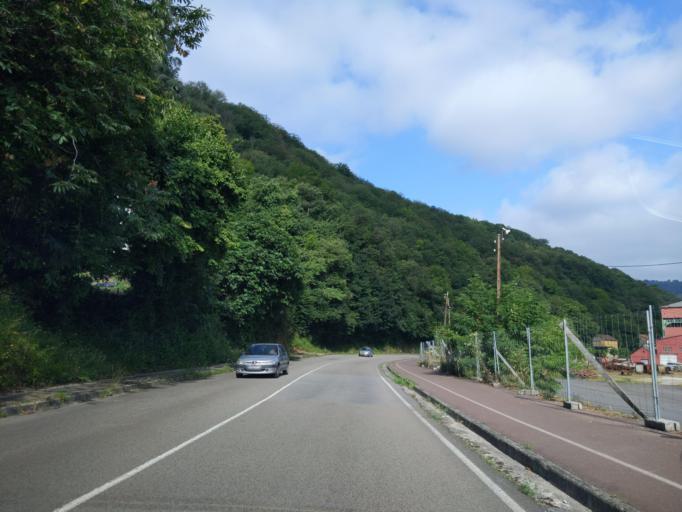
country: ES
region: Asturias
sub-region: Province of Asturias
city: El entrego
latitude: 43.2791
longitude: -5.6200
